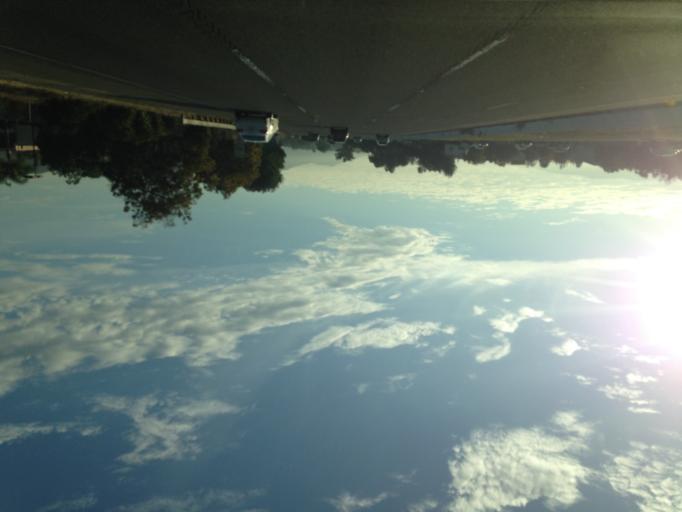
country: US
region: California
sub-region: Riverside County
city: Temecula
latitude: 33.5160
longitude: -117.1589
